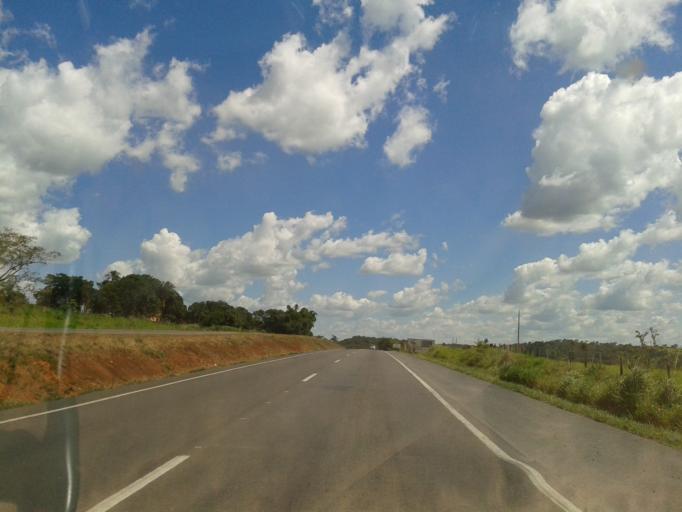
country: BR
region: Goias
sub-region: Piracanjuba
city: Piracanjuba
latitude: -17.3624
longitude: -49.2476
